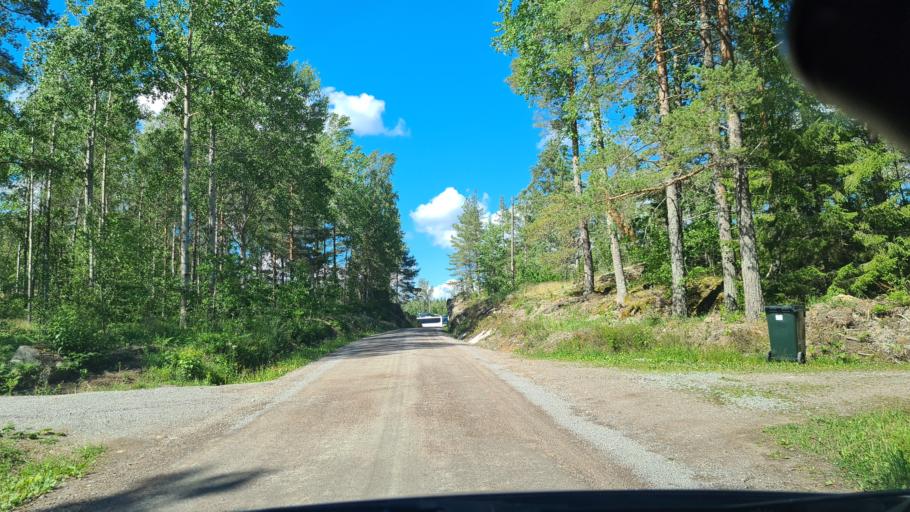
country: SE
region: OEstergoetland
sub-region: Norrkopings Kommun
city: Krokek
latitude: 58.6777
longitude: 16.4289
